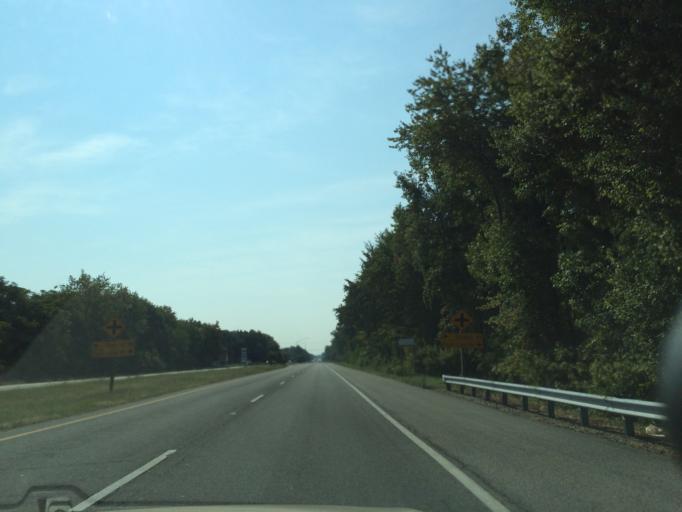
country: US
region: Maryland
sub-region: Charles County
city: La Plata
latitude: 38.4417
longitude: -76.9827
